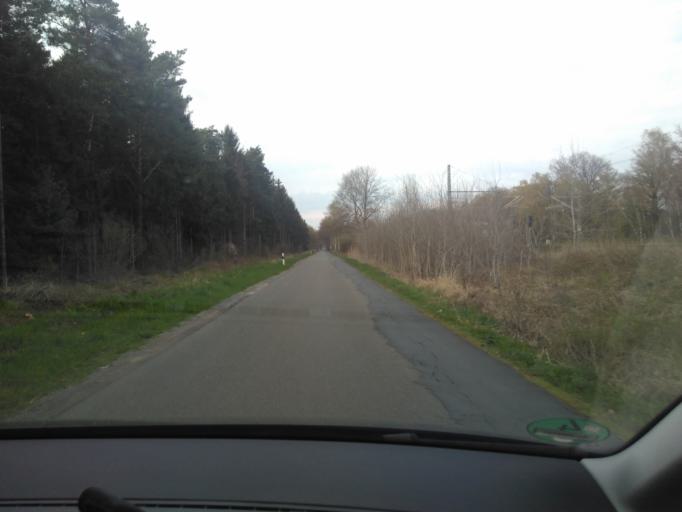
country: DE
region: Lower Saxony
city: Adelheidsdorf
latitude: 52.5317
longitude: 10.0320
